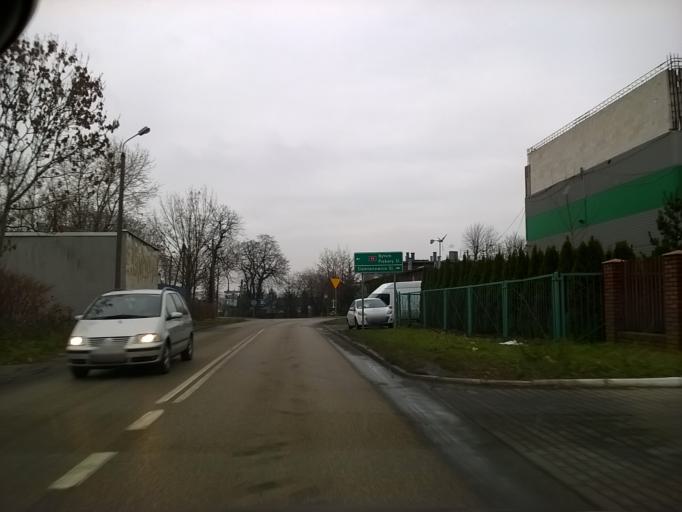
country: PL
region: Silesian Voivodeship
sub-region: Chorzow
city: Chorzow
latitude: 50.3212
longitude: 18.9781
